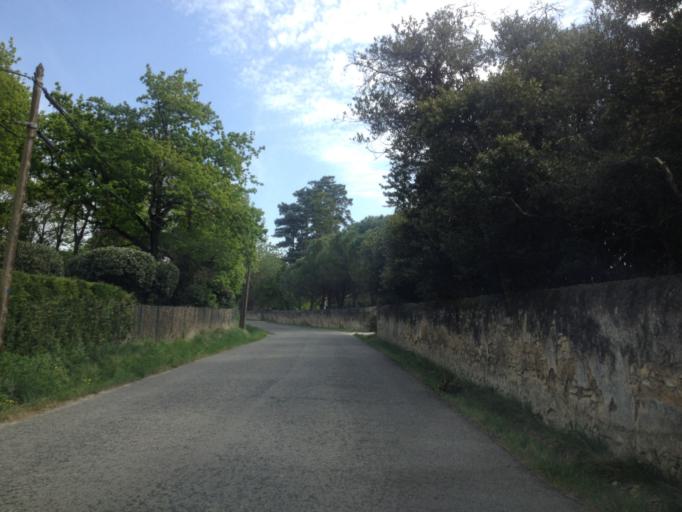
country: FR
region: Provence-Alpes-Cote d'Azur
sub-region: Departement du Vaucluse
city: Orange
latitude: 44.1386
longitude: 4.7900
